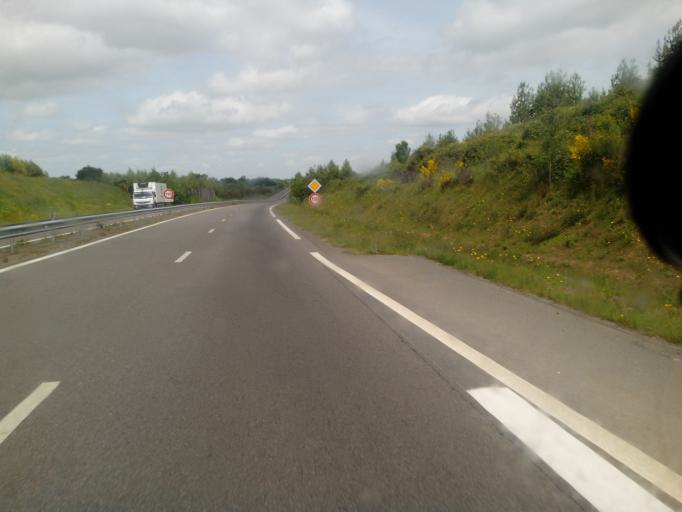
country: FR
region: Brittany
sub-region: Departement d'Ille-et-Vilaine
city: Betton
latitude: 48.1834
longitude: -1.6245
